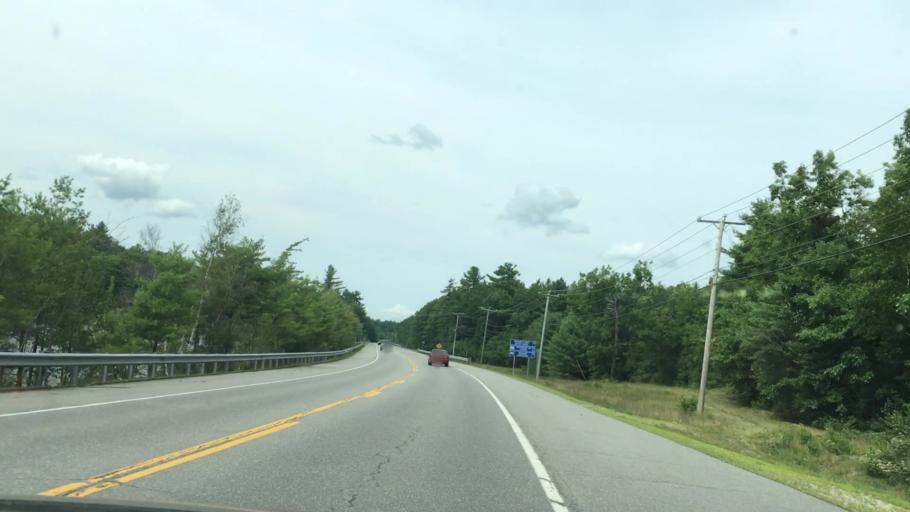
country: US
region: New Hampshire
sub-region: Cheshire County
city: Rindge
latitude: 42.7750
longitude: -72.0329
